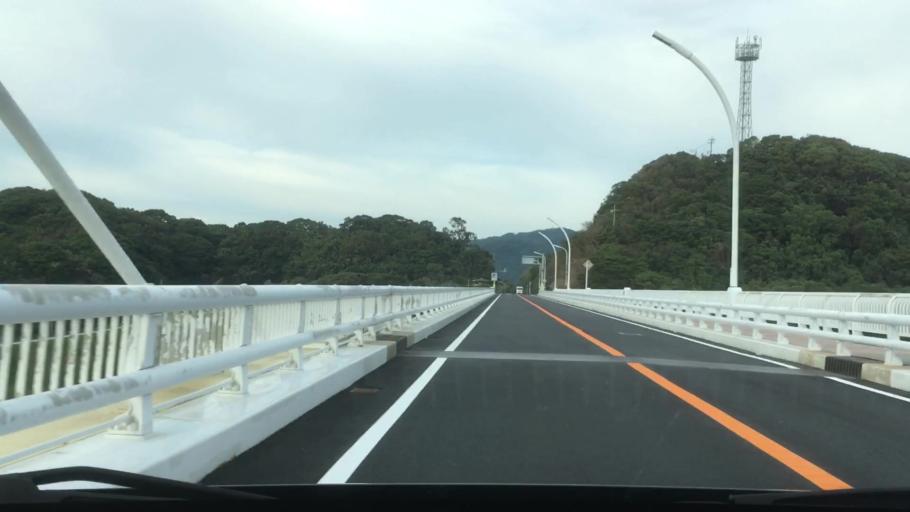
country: JP
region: Nagasaki
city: Sasebo
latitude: 33.0378
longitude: 129.6385
